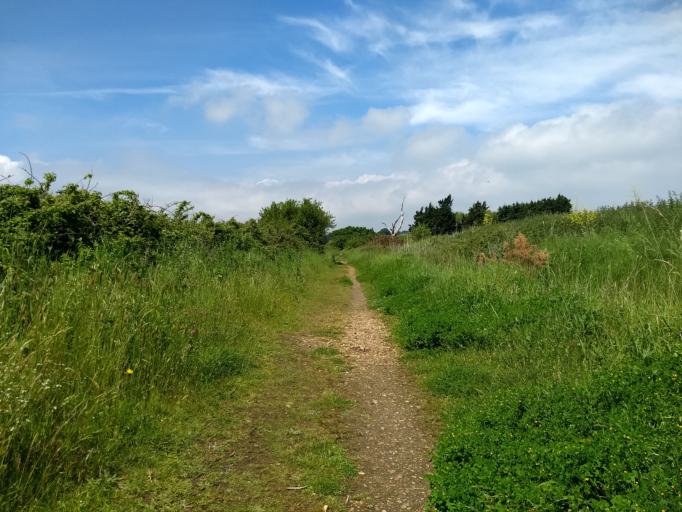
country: GB
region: England
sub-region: Isle of Wight
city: Bembridge
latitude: 50.6913
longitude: -1.1046
